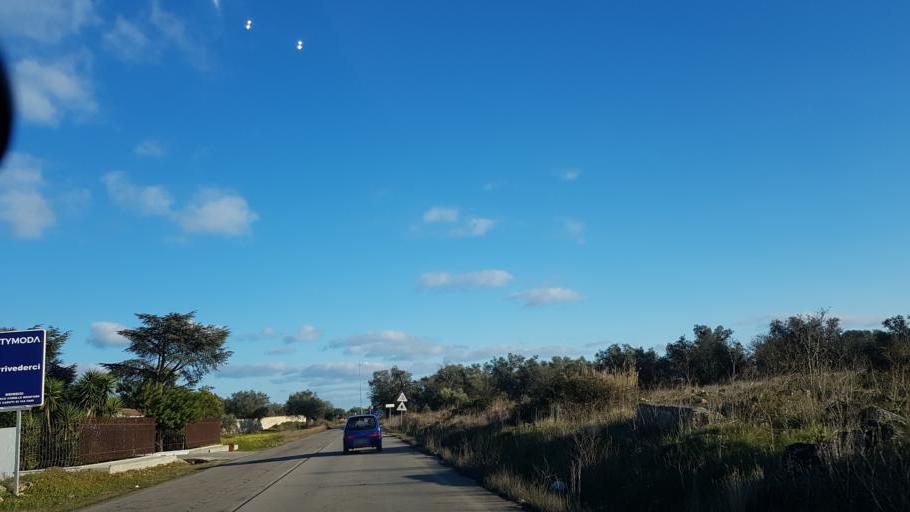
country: IT
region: Apulia
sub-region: Provincia di Brindisi
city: San Pietro Vernotico
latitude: 40.4778
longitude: 18.0042
